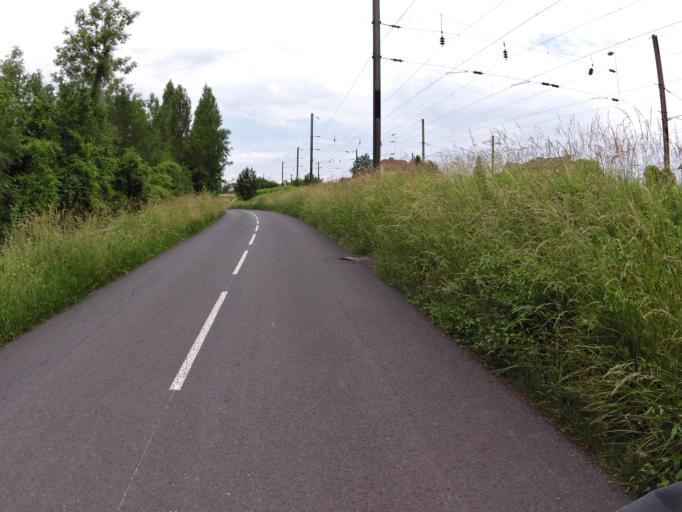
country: FR
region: Champagne-Ardenne
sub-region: Departement des Ardennes
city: Lumes
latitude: 49.7320
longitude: 4.7839
